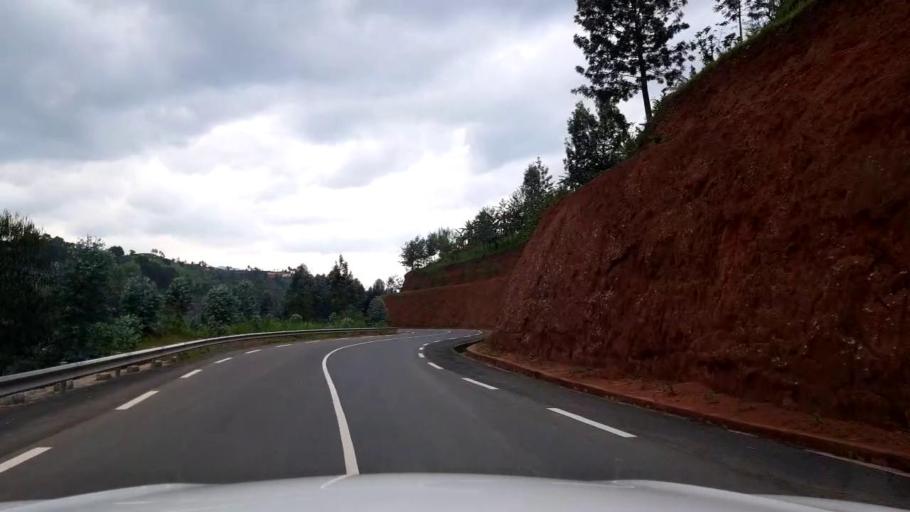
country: RW
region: Western Province
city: Kibuye
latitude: -1.8855
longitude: 29.3460
